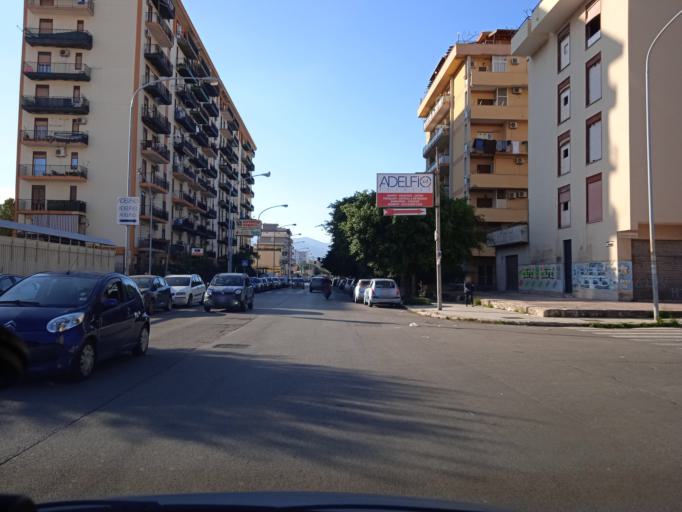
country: IT
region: Sicily
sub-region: Palermo
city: Ciaculli
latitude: 38.1046
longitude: 13.3834
